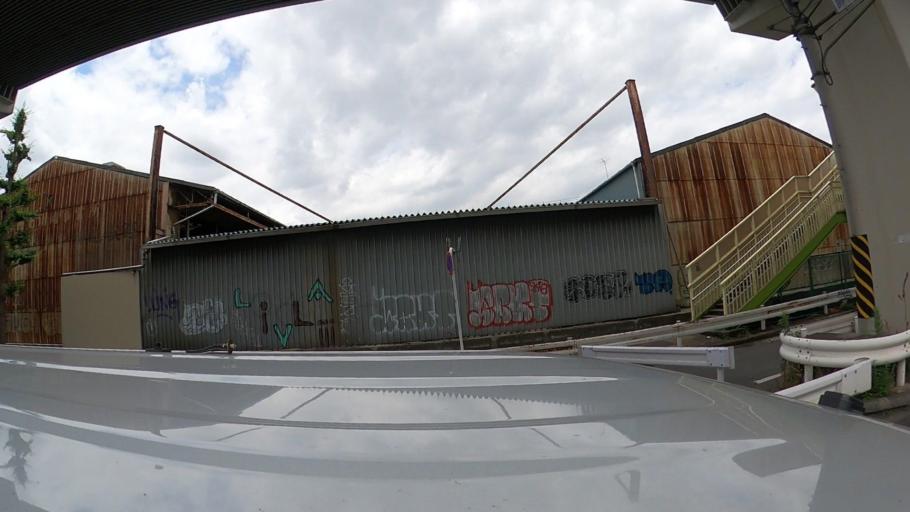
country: JP
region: Kanagawa
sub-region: Kawasaki-shi
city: Kawasaki
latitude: 35.5017
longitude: 139.6979
